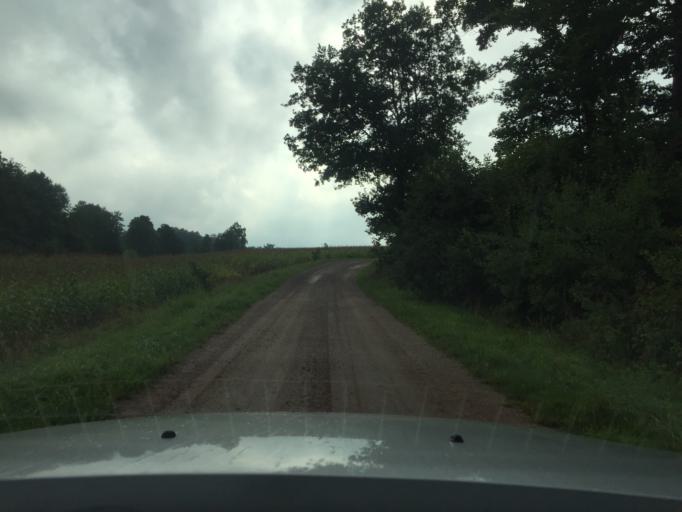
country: SE
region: Skane
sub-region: Hassleholms Kommun
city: Sosdala
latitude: 56.0196
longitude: 13.6710
